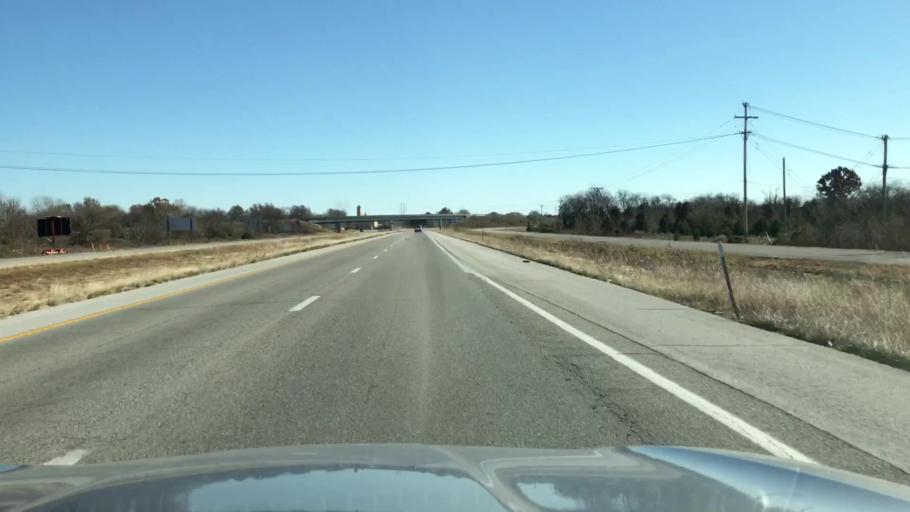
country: US
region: Missouri
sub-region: Jasper County
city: Carthage
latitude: 37.1359
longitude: -94.3176
